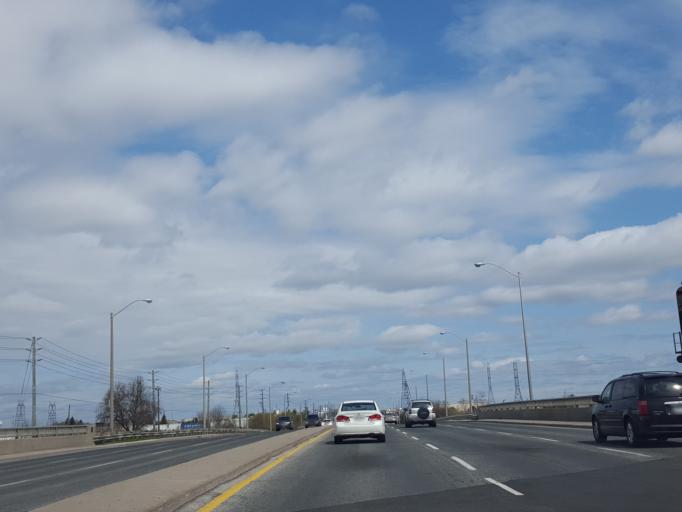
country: CA
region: Ontario
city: Scarborough
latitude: 43.8156
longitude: -79.2441
